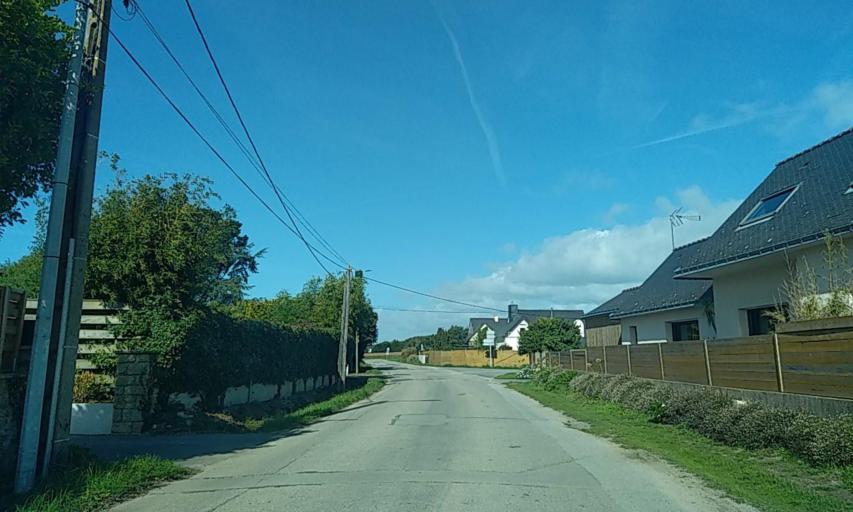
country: FR
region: Brittany
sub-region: Departement du Morbihan
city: Ploemeur
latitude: 47.7161
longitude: -3.4541
